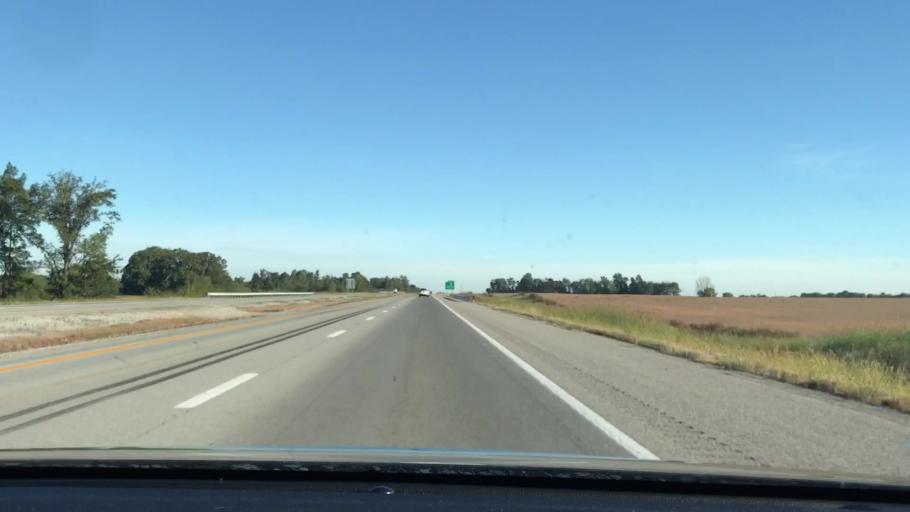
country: US
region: Kentucky
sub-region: Christian County
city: Hopkinsville
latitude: 36.7723
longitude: -87.4987
